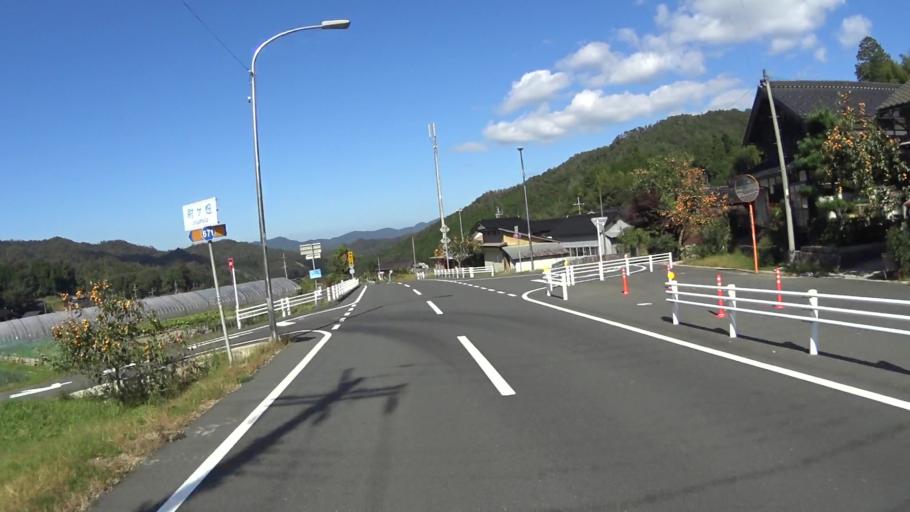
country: JP
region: Hyogo
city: Toyooka
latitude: 35.5438
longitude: 134.9784
